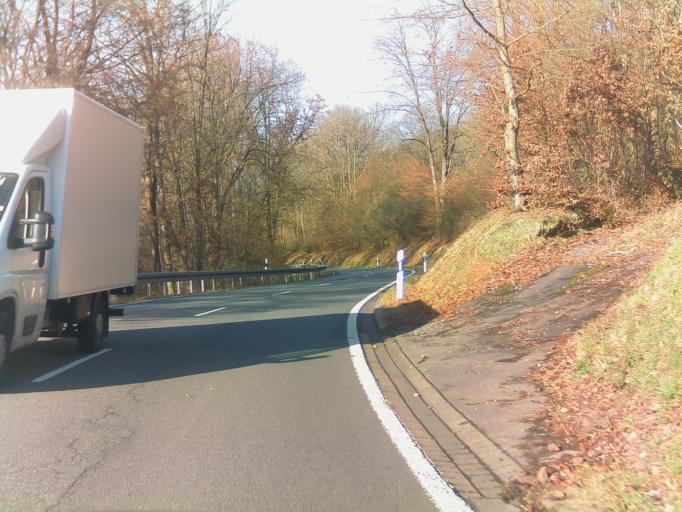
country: DE
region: Baden-Wuerttemberg
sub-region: Regierungsbezirk Stuttgart
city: Freudenberg
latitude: 49.7797
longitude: 9.3210
